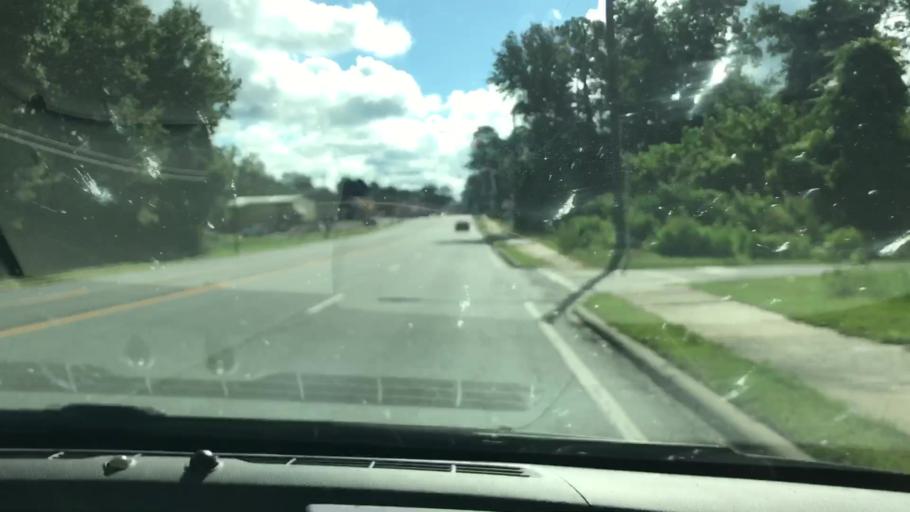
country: US
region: Georgia
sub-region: Worth County
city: Sylvester
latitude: 31.5310
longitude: -83.8471
